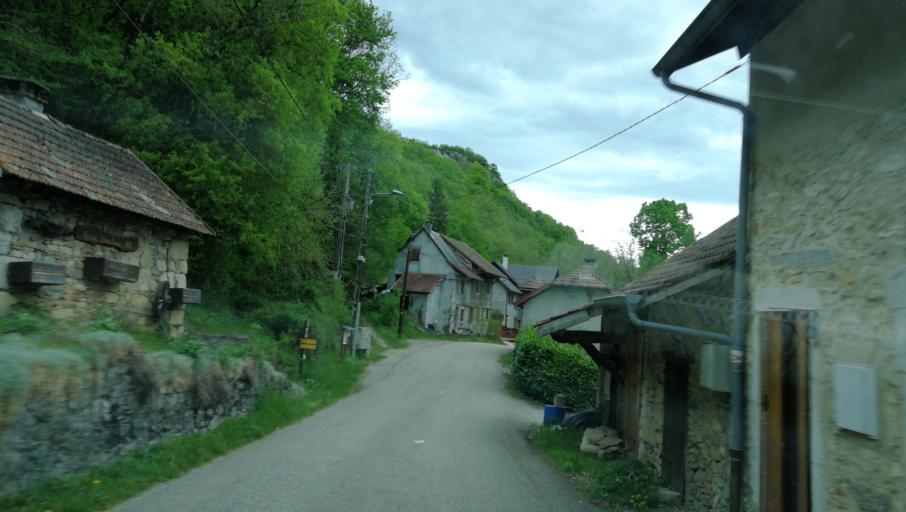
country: FR
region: Rhone-Alpes
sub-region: Departement de la Savoie
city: Chatillon
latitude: 45.7675
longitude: 5.8232
